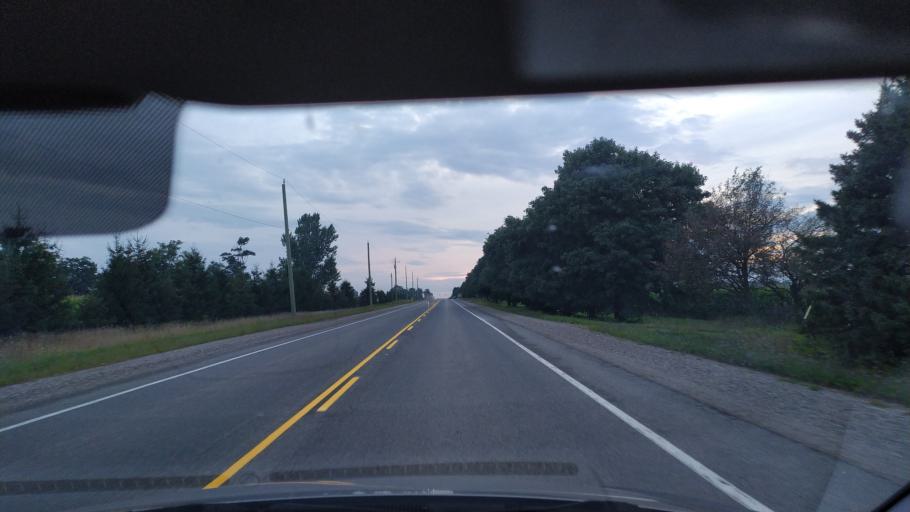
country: CA
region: Ontario
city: Kitchener
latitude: 43.3250
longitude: -80.4858
